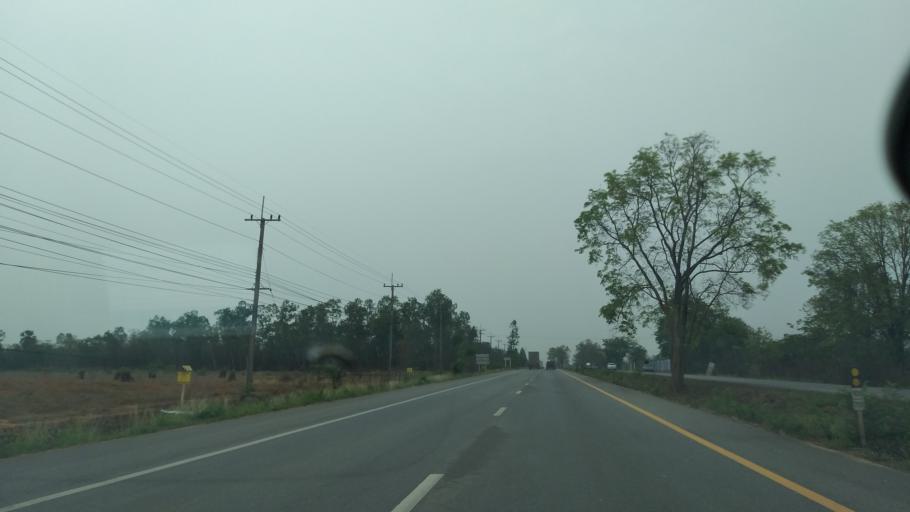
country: TH
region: Chachoengsao
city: Plaeng Yao
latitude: 13.5062
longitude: 101.2698
